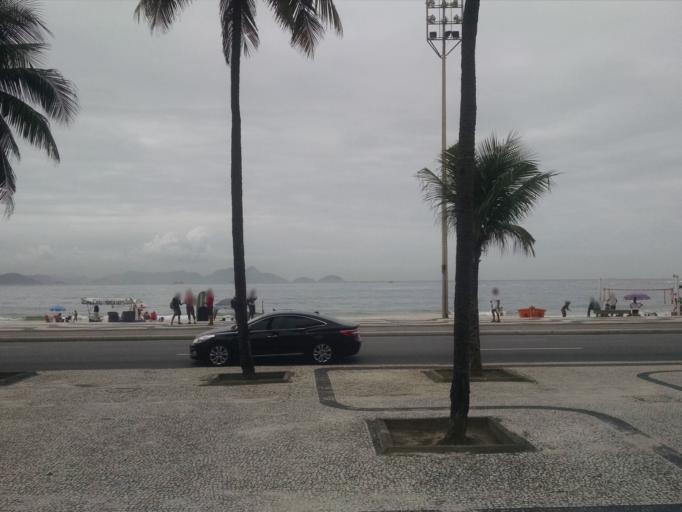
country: BR
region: Rio de Janeiro
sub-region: Rio De Janeiro
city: Rio de Janeiro
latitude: -22.9812
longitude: -43.1899
